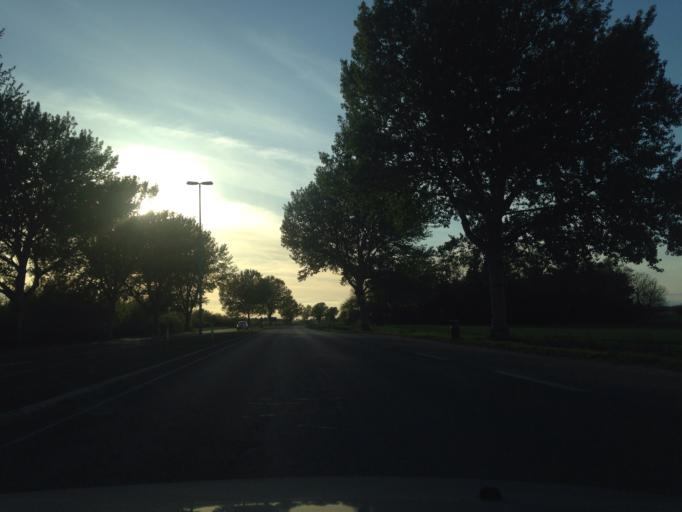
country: DK
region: Zealand
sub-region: Greve Kommune
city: Greve
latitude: 55.5898
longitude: 12.2462
